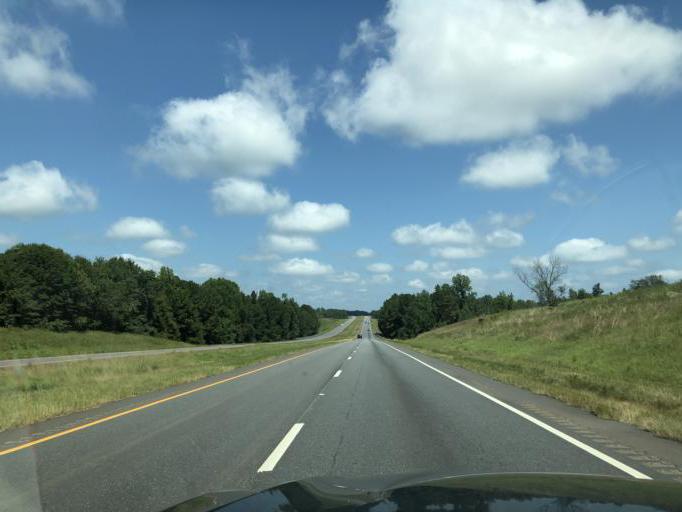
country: US
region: Alabama
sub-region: Henry County
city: Abbeville
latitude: 31.5161
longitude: -85.2909
